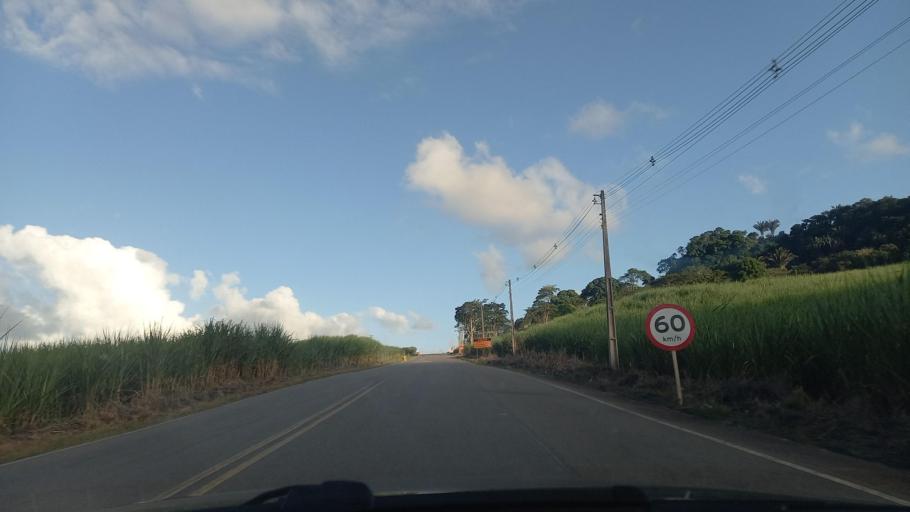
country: BR
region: Alagoas
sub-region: Sao Miguel Dos Campos
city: Sao Miguel dos Campos
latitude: -9.8152
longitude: -36.2208
